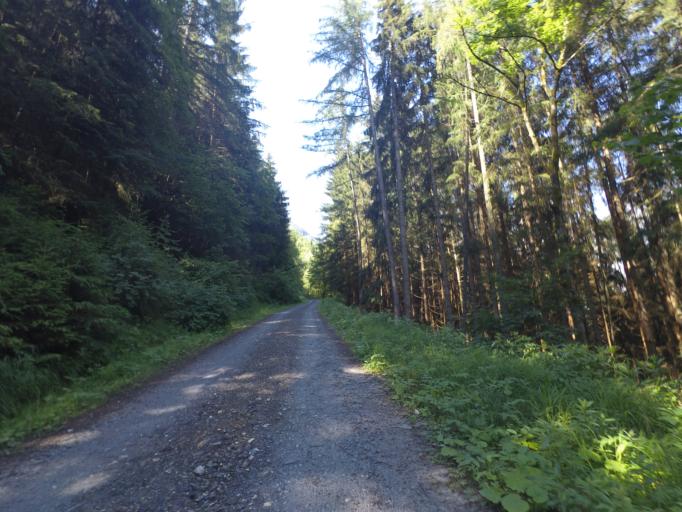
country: AT
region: Salzburg
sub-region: Politischer Bezirk Sankt Johann im Pongau
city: Schwarzach im Pongau
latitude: 47.3054
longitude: 13.1423
